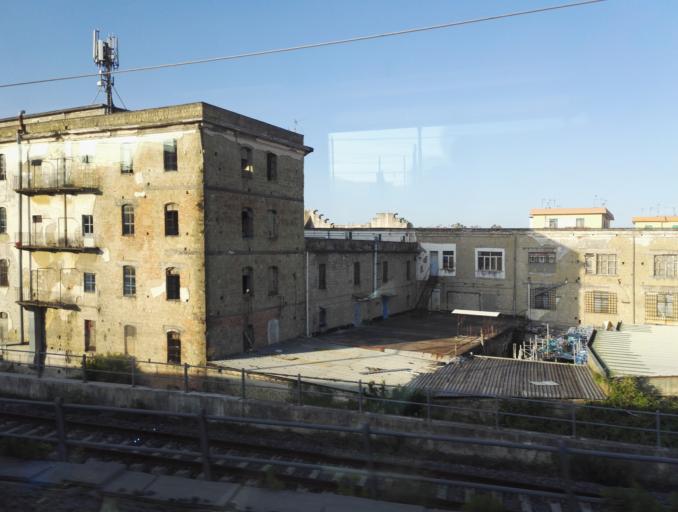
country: IT
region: Campania
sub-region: Provincia di Napoli
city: Arpino
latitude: 40.8630
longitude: 14.2963
